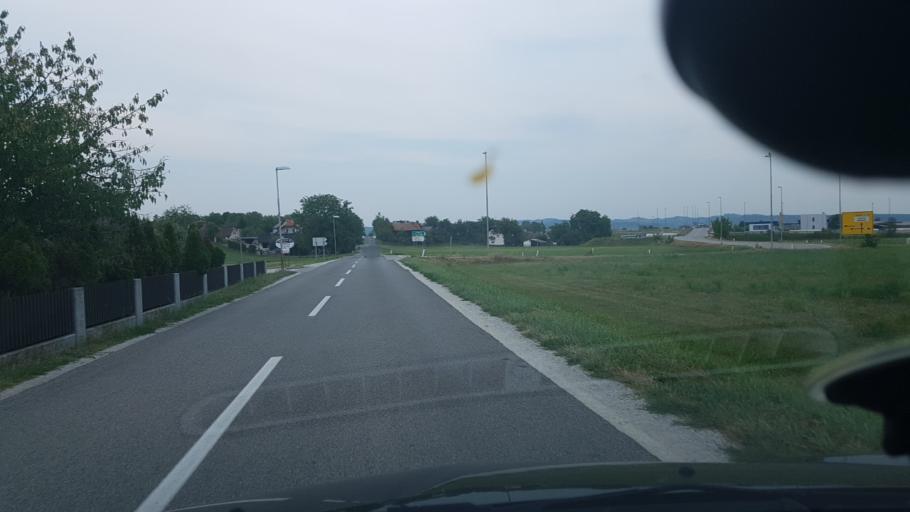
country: HR
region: Zagrebacka
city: Bregana
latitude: 45.8458
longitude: 15.6877
